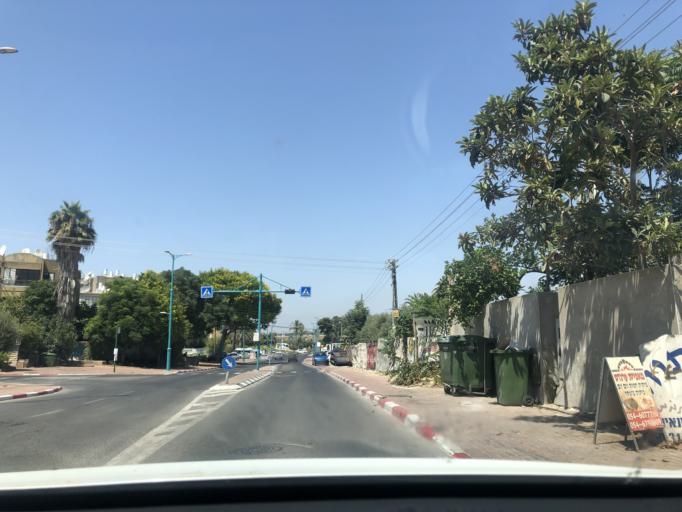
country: IL
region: Central District
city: Lod
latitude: 31.9530
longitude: 34.9035
